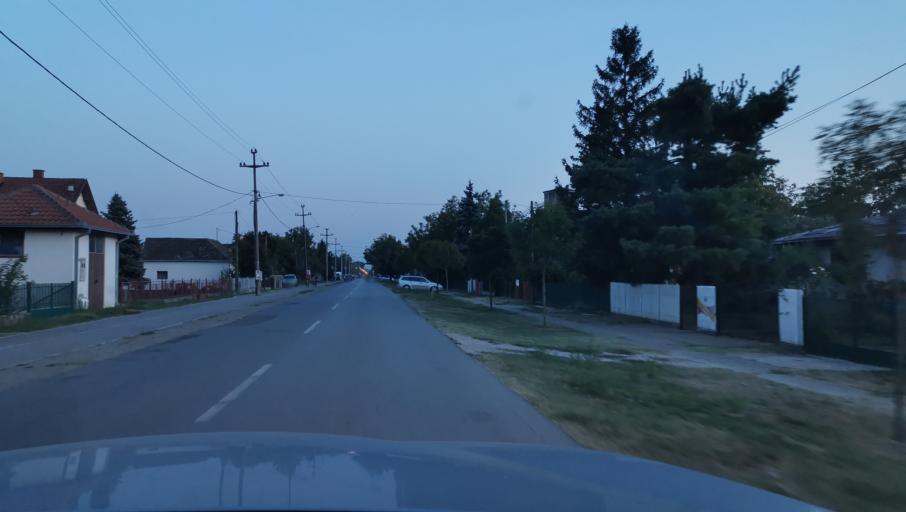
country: RS
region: Central Serbia
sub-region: Belgrade
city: Obrenovac
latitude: 44.6812
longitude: 20.2022
